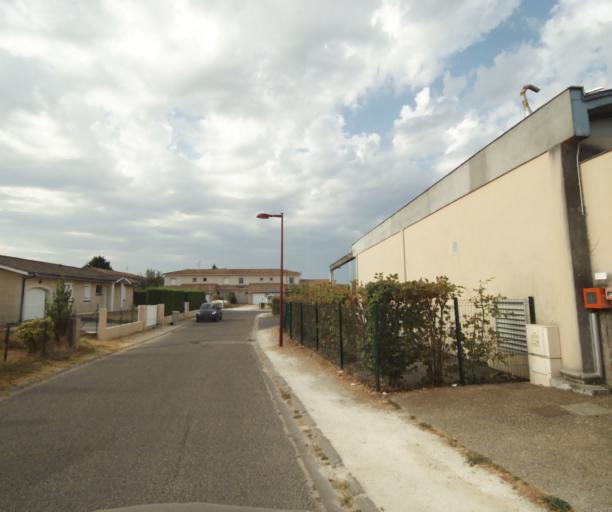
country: FR
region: Aquitaine
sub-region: Departement de la Gironde
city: Creon
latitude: 44.7712
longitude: -0.3478
